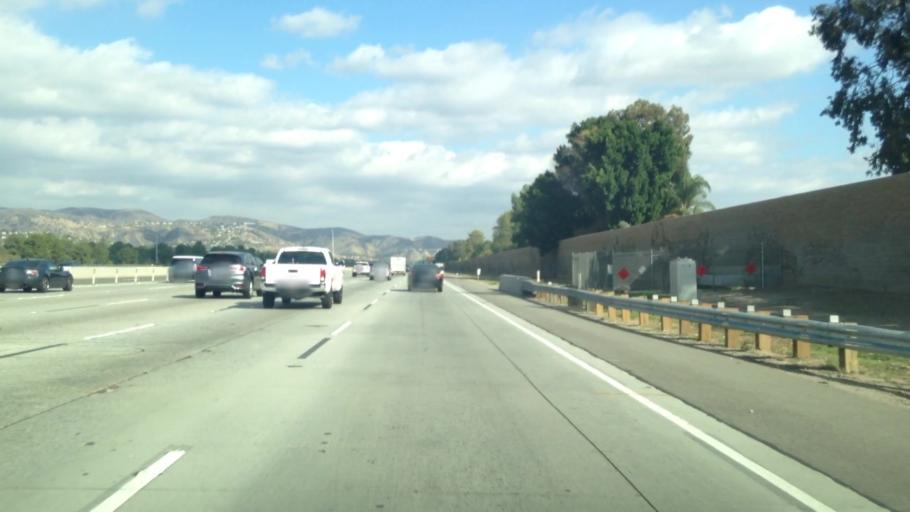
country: US
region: California
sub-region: Orange County
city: Yorba Linda
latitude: 33.8585
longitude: -117.7805
